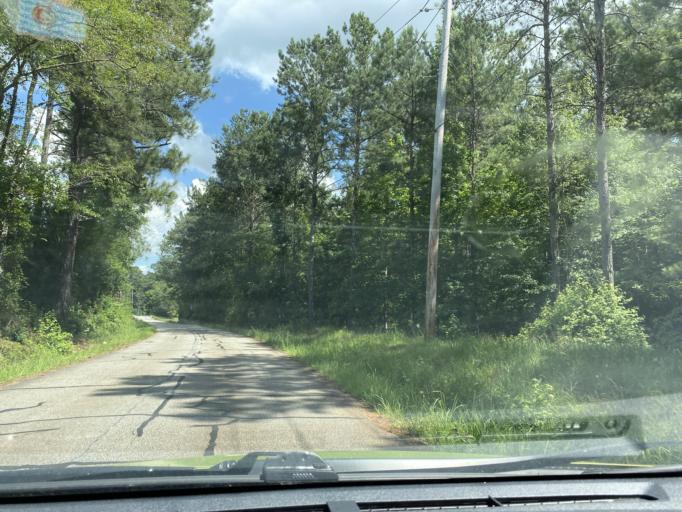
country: US
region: Georgia
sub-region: Fulton County
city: Palmetto
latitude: 33.4258
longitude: -84.7056
